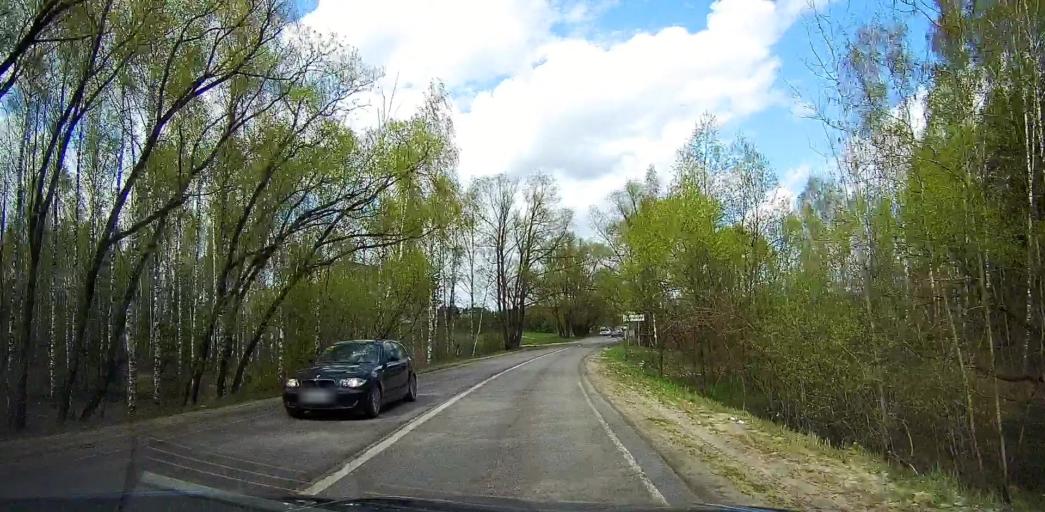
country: RU
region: Moskovskaya
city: Davydovo
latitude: 55.6072
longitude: 38.8475
